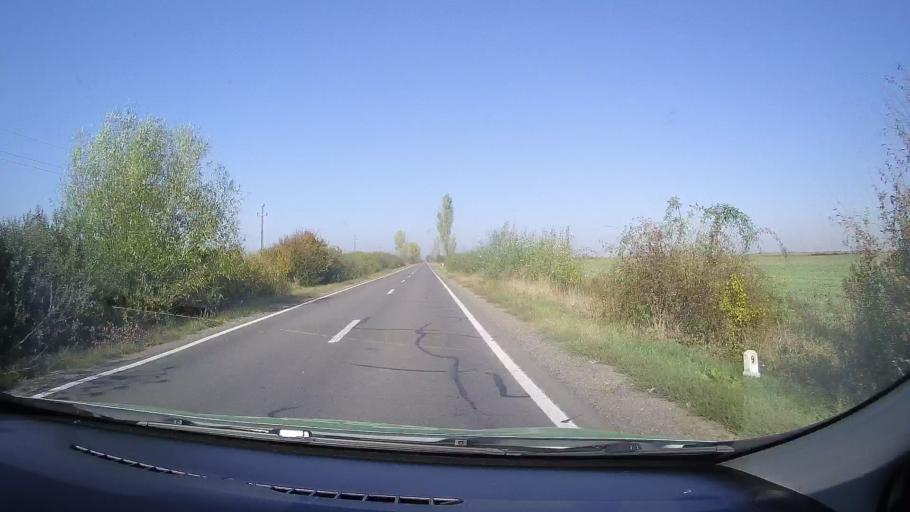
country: RO
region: Satu Mare
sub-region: Comuna Urziceni
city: Urziceni
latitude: 47.7086
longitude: 22.4297
